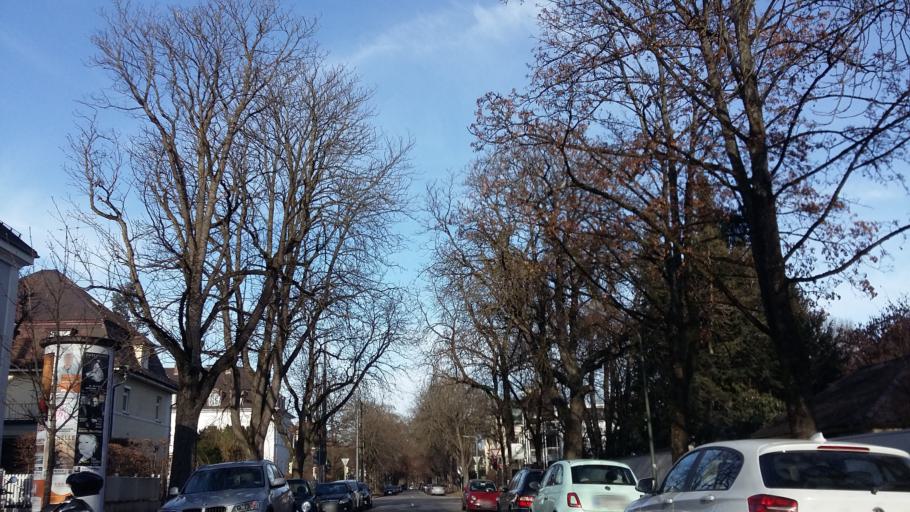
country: DE
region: Bavaria
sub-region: Upper Bavaria
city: Munich
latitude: 48.1553
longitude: 11.5199
